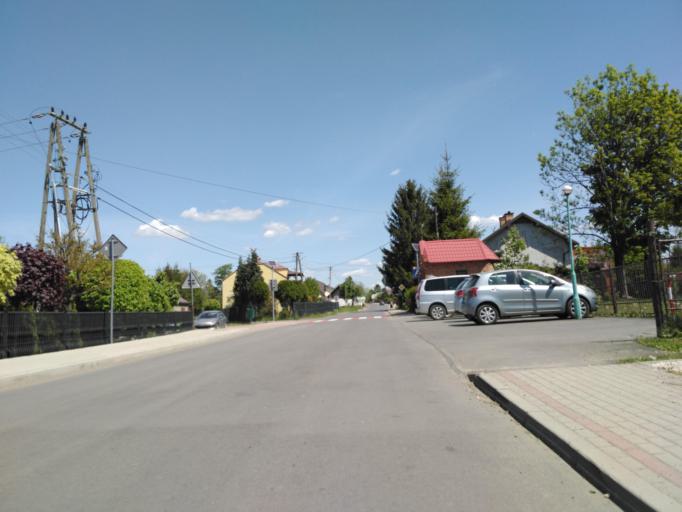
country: PL
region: Subcarpathian Voivodeship
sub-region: Powiat krosnienski
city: Chorkowka
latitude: 49.6757
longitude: 21.6943
